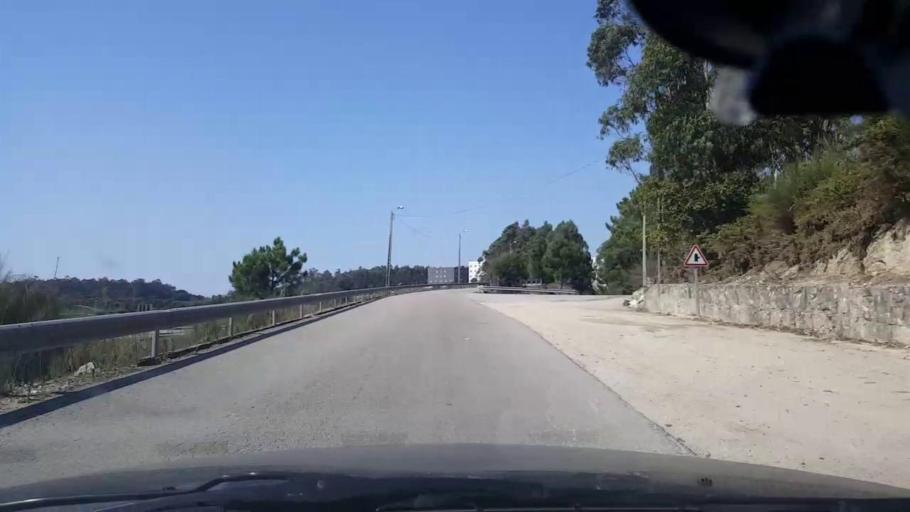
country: PT
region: Porto
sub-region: Vila do Conde
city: Vila do Conde
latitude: 41.3831
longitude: -8.7090
